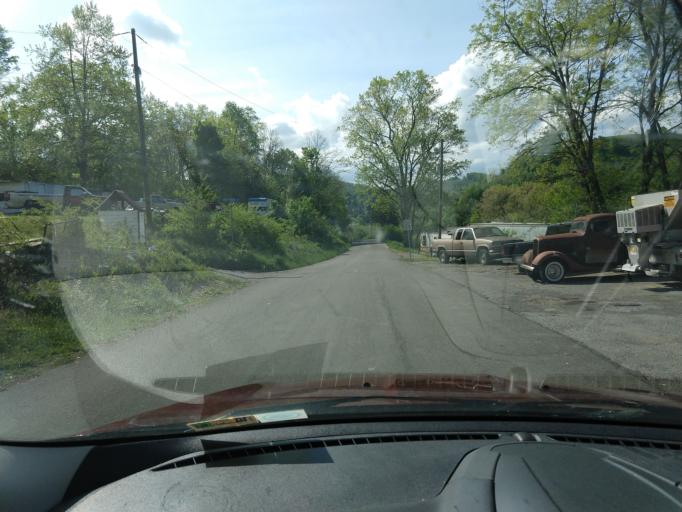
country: US
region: Virginia
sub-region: Russell County
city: Honaker
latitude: 37.0193
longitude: -81.9719
